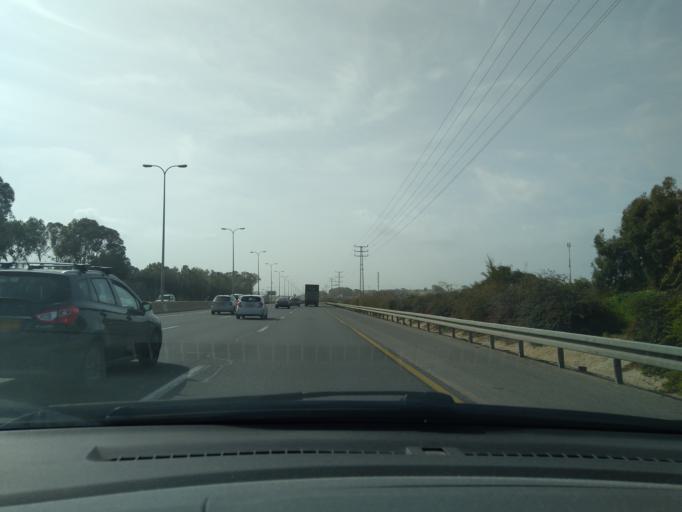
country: IL
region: Central District
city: Netanya
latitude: 32.3104
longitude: 34.8653
